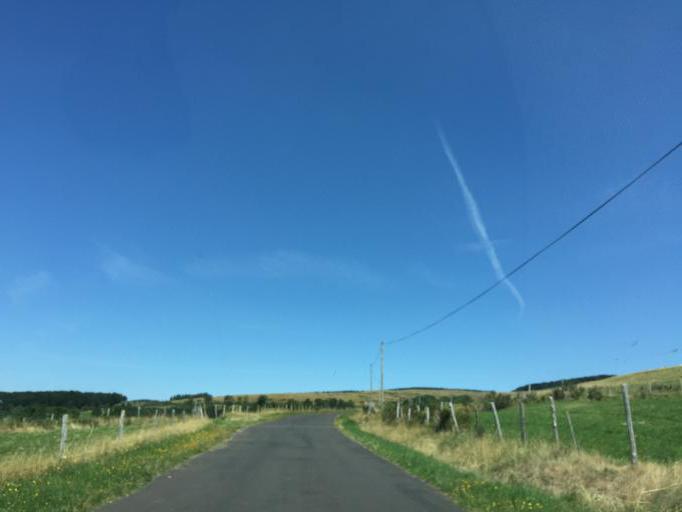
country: FR
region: Midi-Pyrenees
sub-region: Departement de l'Aveyron
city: Laguiole
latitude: 44.6508
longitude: 2.8844
